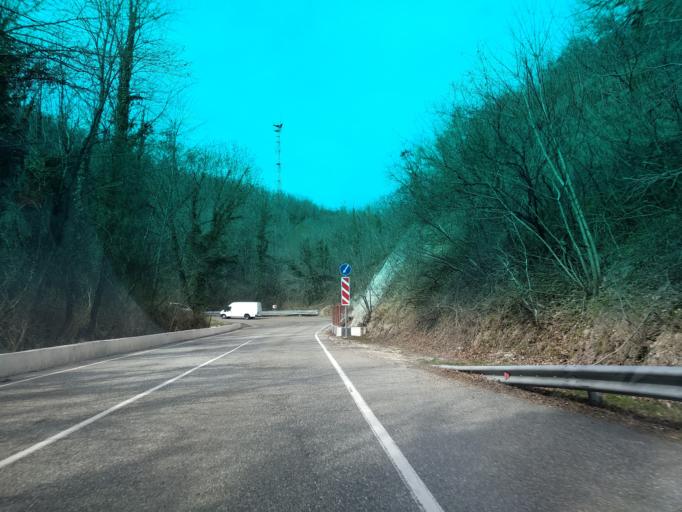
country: RU
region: Krasnodarskiy
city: Shepsi
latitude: 44.0497
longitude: 39.1347
